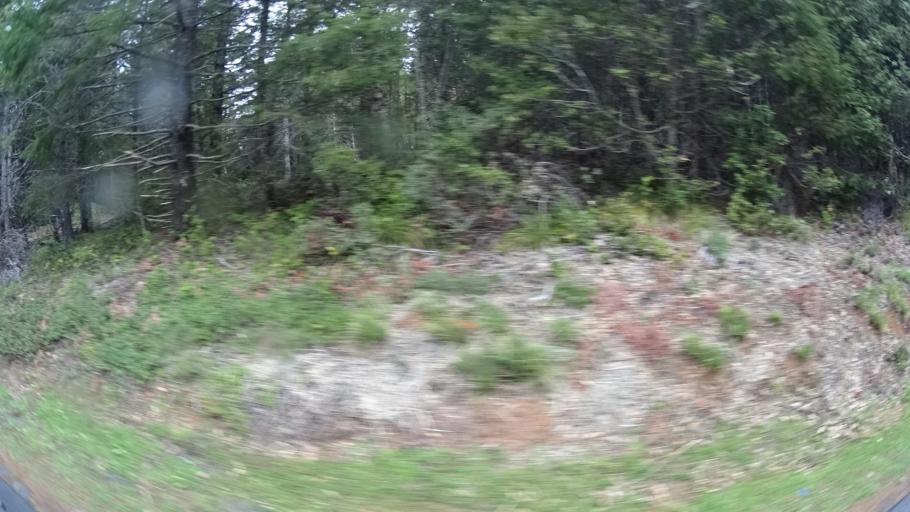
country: US
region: California
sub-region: Humboldt County
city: Willow Creek
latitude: 41.1985
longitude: -123.8064
